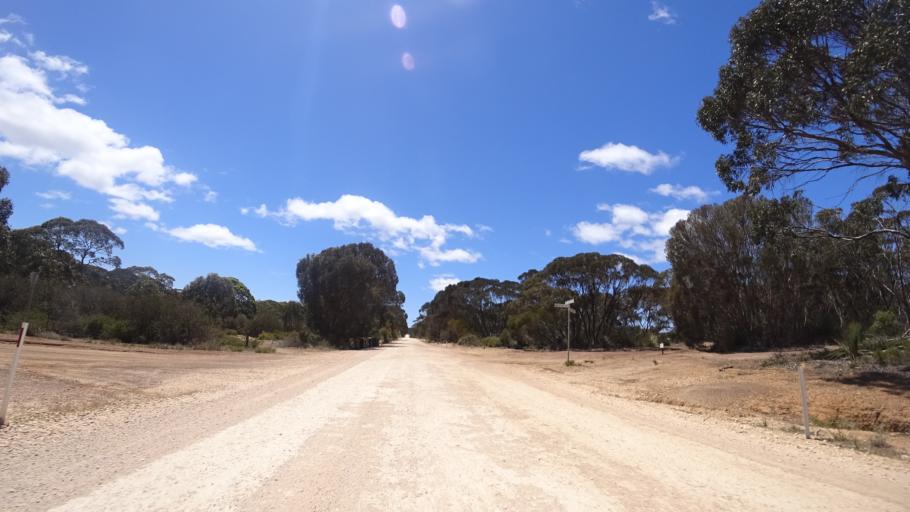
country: AU
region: South Australia
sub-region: Kangaroo Island
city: Kingscote
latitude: -35.8262
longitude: 138.0141
